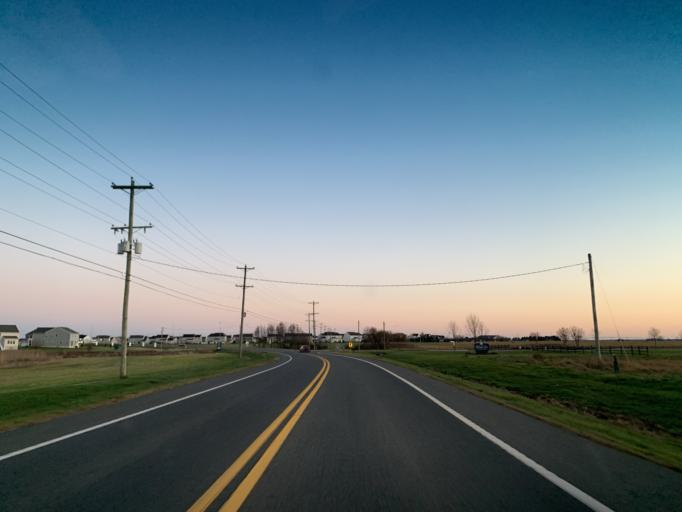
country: US
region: Delaware
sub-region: New Castle County
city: Middletown
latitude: 39.4308
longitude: -75.7423
